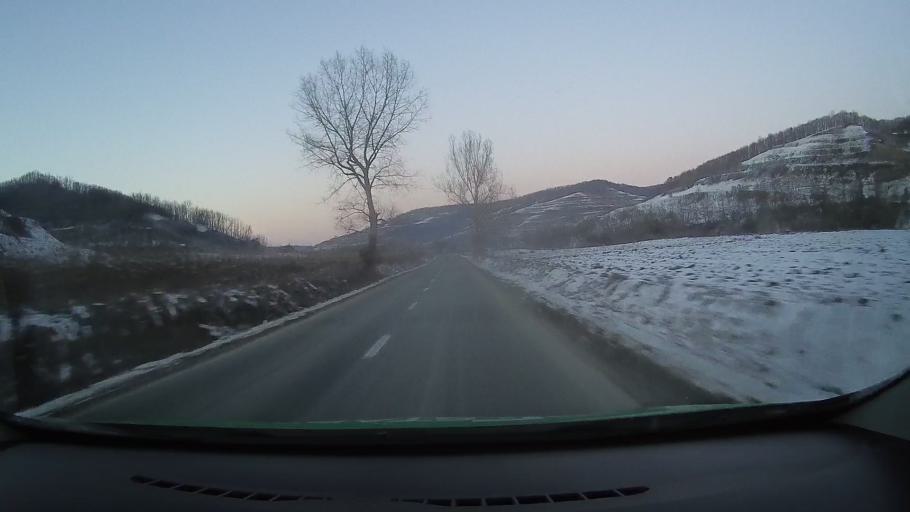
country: RO
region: Sibiu
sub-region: Comuna Atel
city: Atel
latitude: 46.1733
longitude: 24.4706
